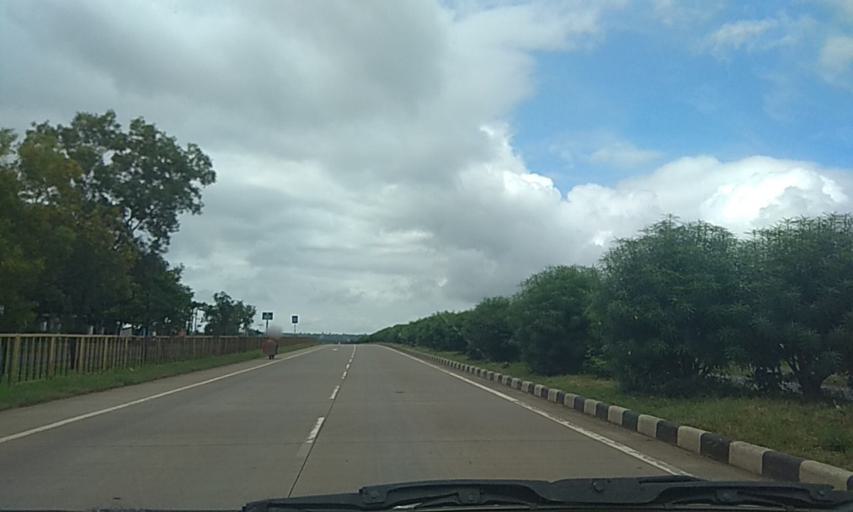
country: IN
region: Karnataka
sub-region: Belgaum
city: Sankeshwar
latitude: 16.3104
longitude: 74.4297
